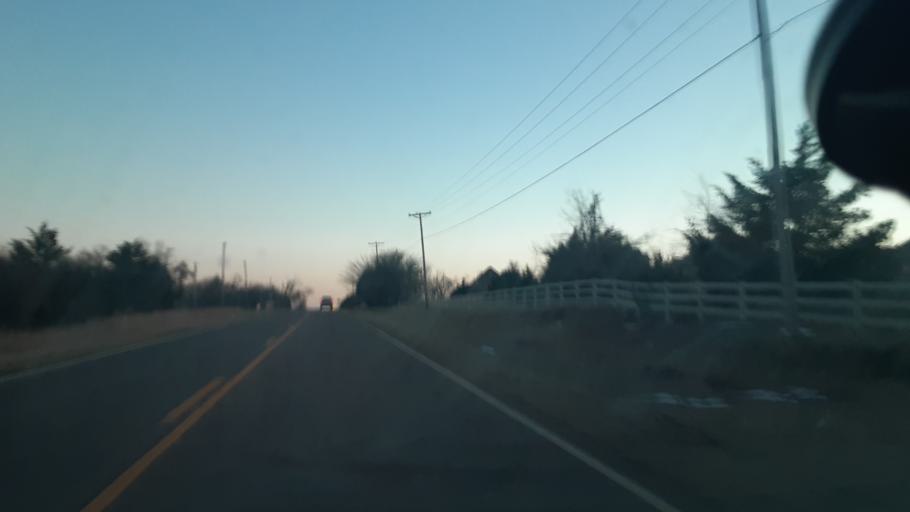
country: US
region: Oklahoma
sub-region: Oklahoma County
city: Edmond
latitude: 35.7150
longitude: -97.4252
